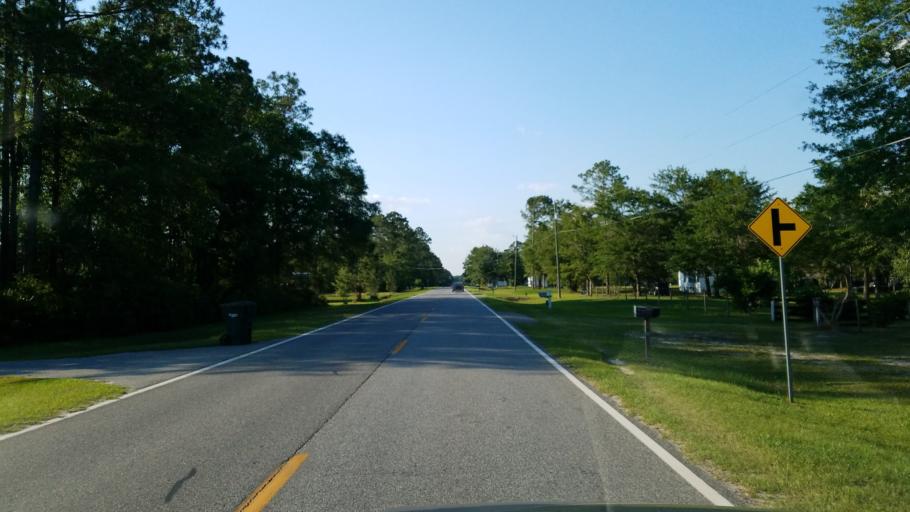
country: US
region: Georgia
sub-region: Lanier County
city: Lakeland
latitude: 30.9505
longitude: -83.0818
